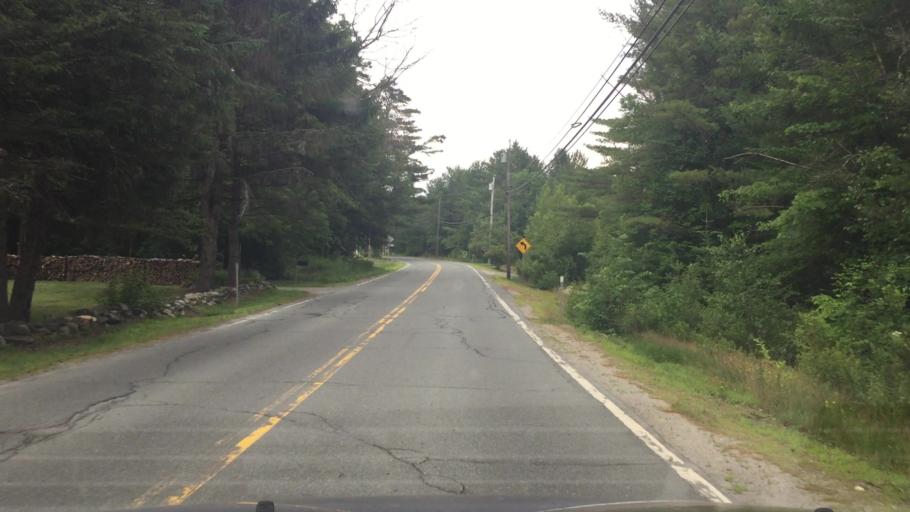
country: US
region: New Hampshire
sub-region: Grafton County
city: Littleton
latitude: 44.2425
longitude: -71.7614
